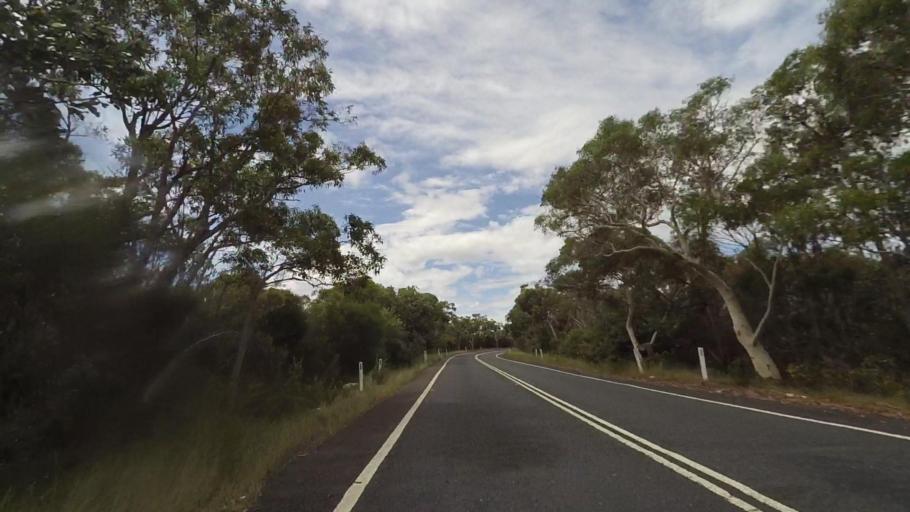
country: AU
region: New South Wales
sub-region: Sutherland Shire
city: Grays Point
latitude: -34.0903
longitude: 151.0642
